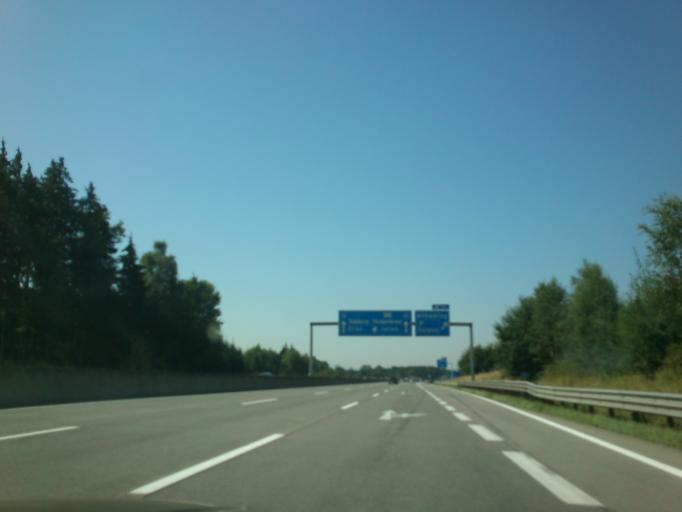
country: AT
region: Upper Austria
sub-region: Wels-Land
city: Marchtrenk
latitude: 48.1605
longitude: 14.1628
